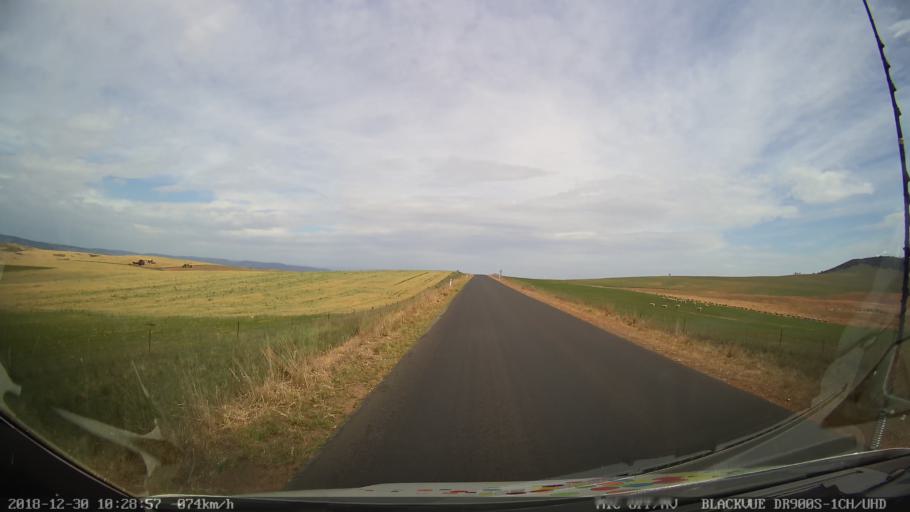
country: AU
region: New South Wales
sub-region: Snowy River
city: Berridale
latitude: -36.5038
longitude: 148.9153
